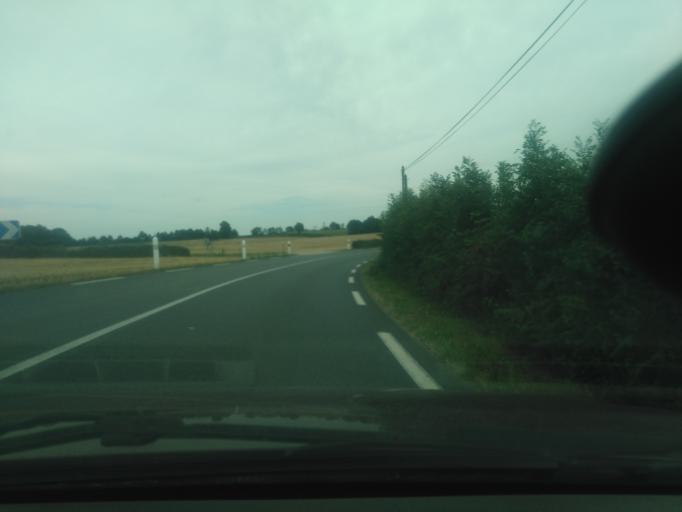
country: FR
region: Poitou-Charentes
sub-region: Departement des Deux-Sevres
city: Moncoutant
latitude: 46.6471
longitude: -0.6112
